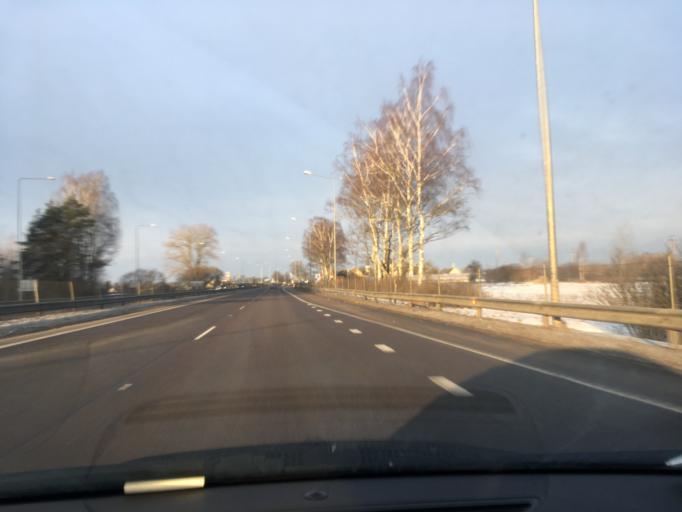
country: LT
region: Vilnius County
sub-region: Vilniaus Rajonas
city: Vievis
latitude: 54.7686
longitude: 24.8359
